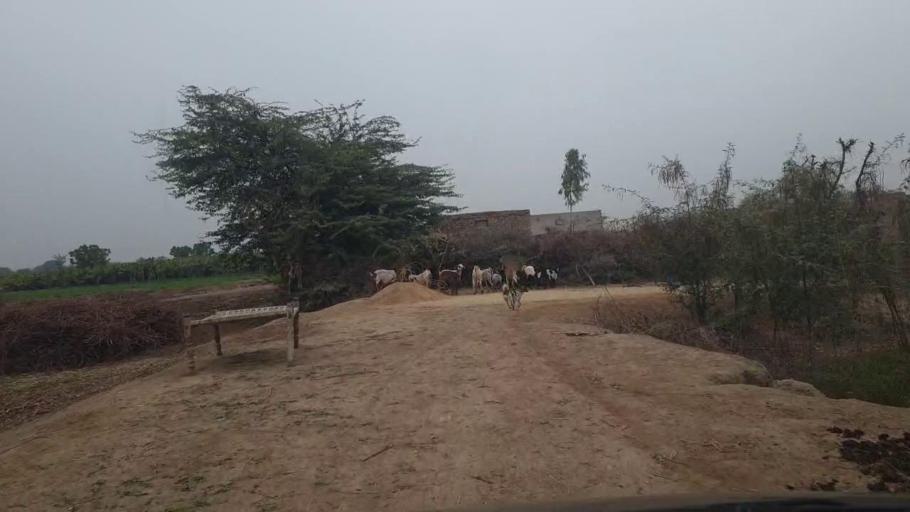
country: PK
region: Sindh
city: Tando Adam
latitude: 25.8298
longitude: 68.6786
